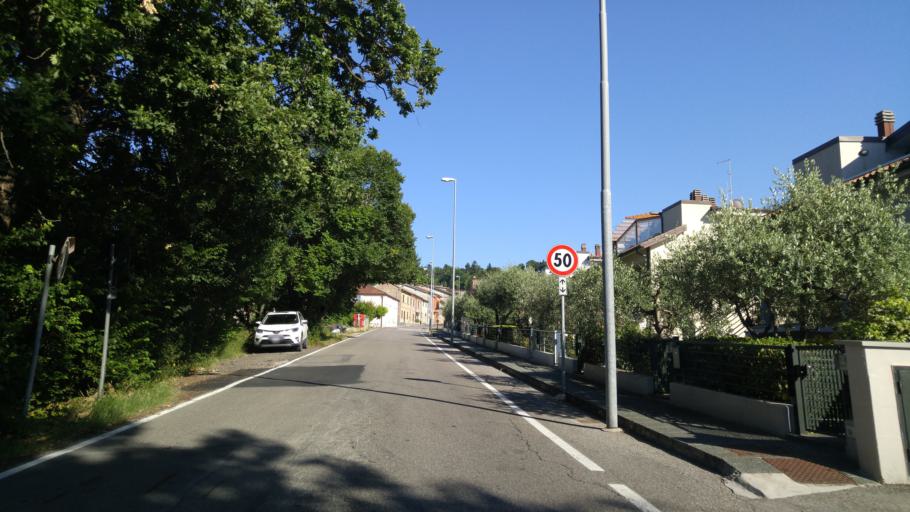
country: IT
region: The Marches
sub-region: Provincia di Pesaro e Urbino
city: Pesaro
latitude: 43.8691
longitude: 12.8998
